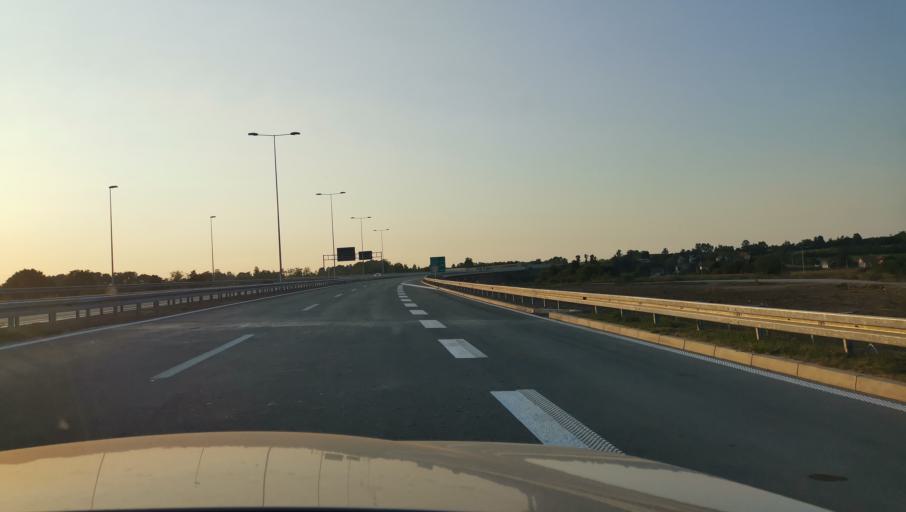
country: RS
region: Central Serbia
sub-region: Kolubarski Okrug
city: Lajkovac
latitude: 44.3594
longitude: 20.1256
